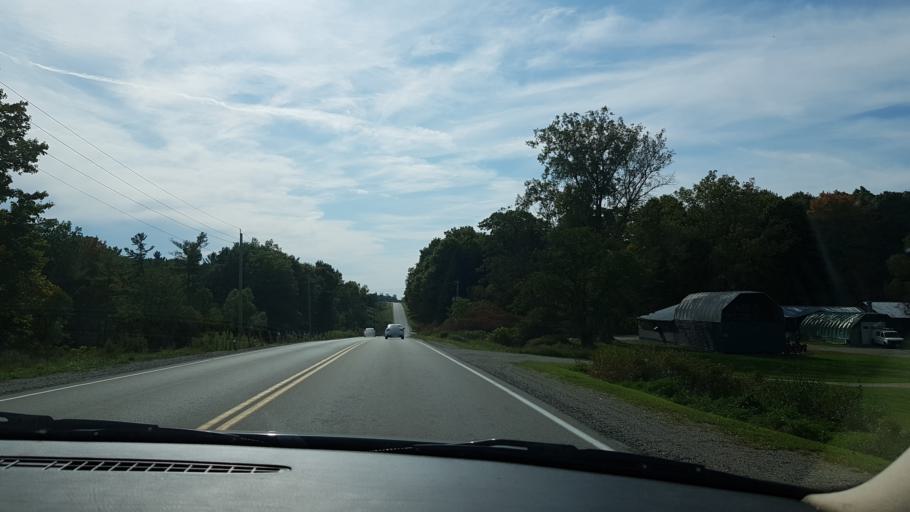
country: CA
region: Ontario
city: Delaware
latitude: 42.9654
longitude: -81.4036
